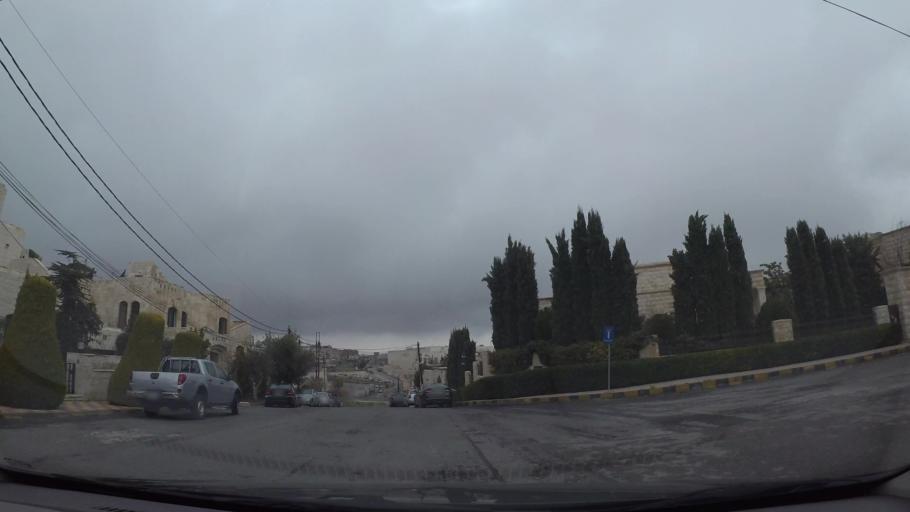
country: JO
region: Amman
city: Al Bunayyat ash Shamaliyah
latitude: 31.9388
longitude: 35.8866
